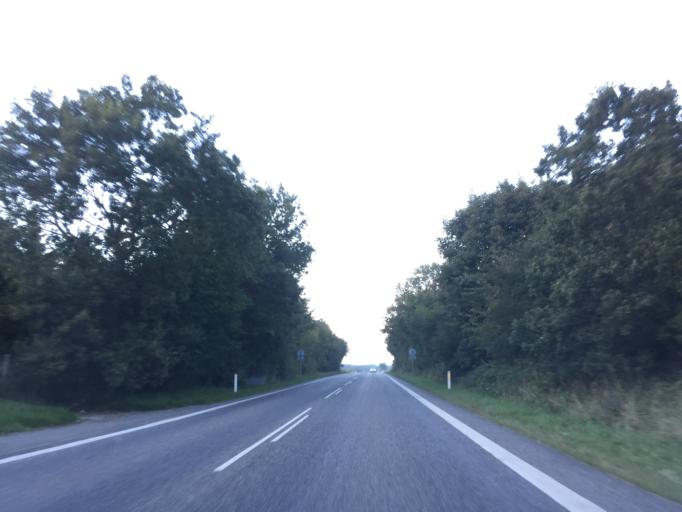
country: DK
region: South Denmark
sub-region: Aabenraa Kommune
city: Lojt Kirkeby
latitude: 55.0856
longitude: 9.4321
